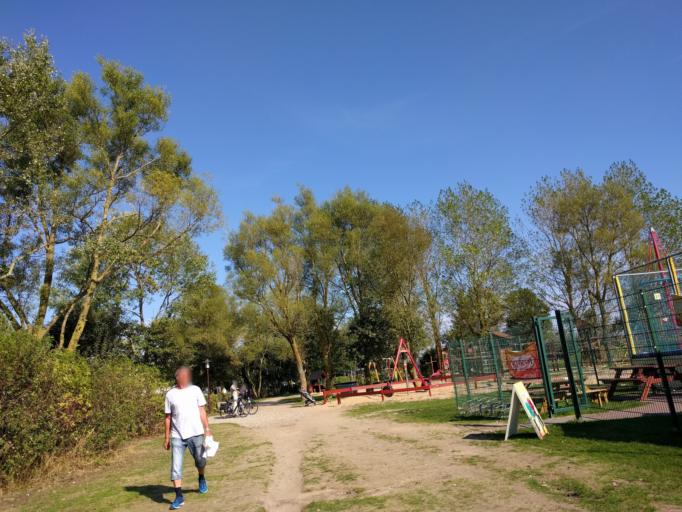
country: DE
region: Schleswig-Holstein
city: Burg auf Fehmarn
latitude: 54.4022
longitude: 11.1741
